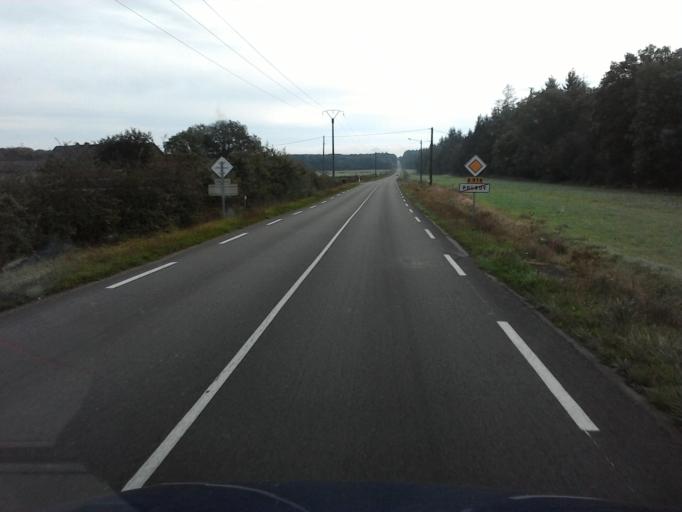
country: FR
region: Bourgogne
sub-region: Departement de Saone-et-Loire
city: Autun
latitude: 47.0036
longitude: 4.2088
